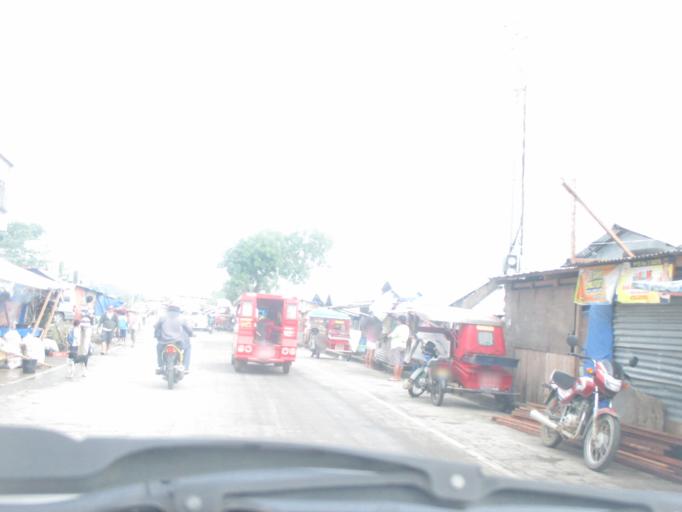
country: PH
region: Eastern Visayas
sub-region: Province of Leyte
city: Panalanoy
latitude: 11.2492
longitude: 124.9936
